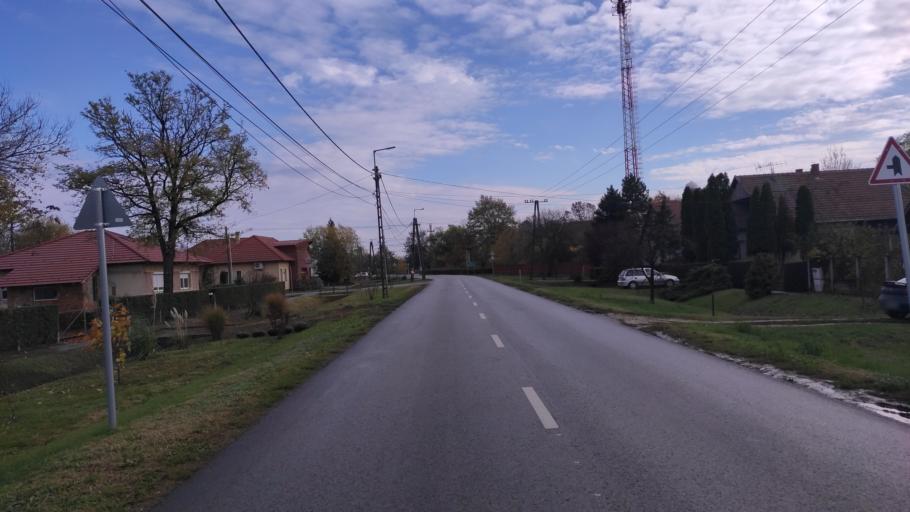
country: HU
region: Bekes
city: Mezobereny
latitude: 46.7617
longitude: 21.0396
